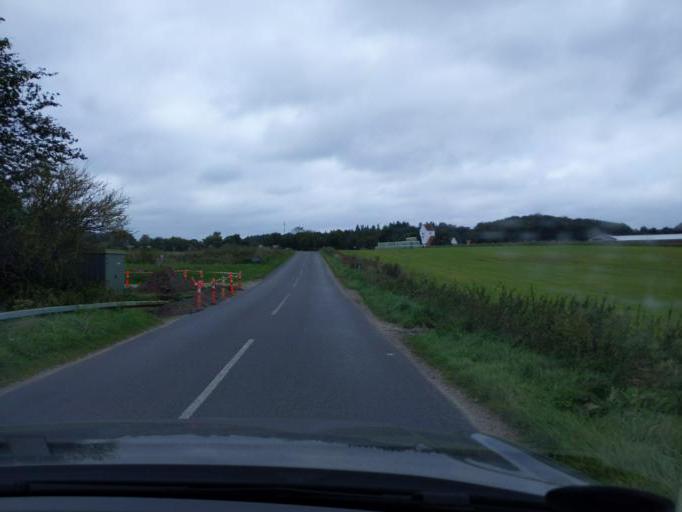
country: DK
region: North Denmark
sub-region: Mariagerfjord Kommune
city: Hobro
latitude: 56.5590
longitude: 9.6908
